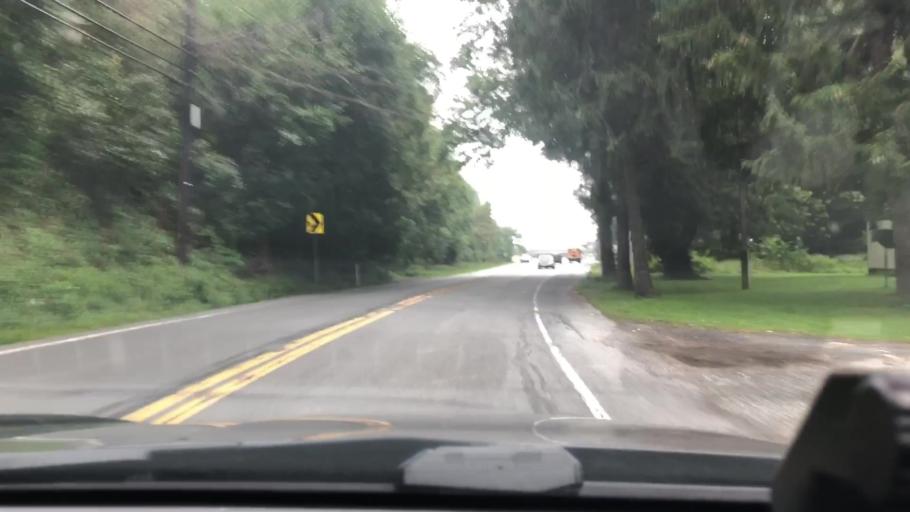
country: US
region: Pennsylvania
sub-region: Berks County
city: Kutztown
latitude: 40.5317
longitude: -75.7826
